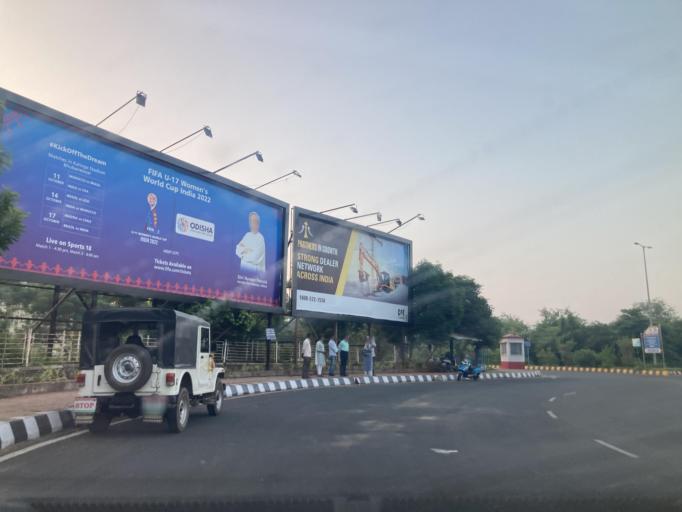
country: IN
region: Odisha
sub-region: Khordha
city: Bhubaneshwar
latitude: 20.2537
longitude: 85.8202
